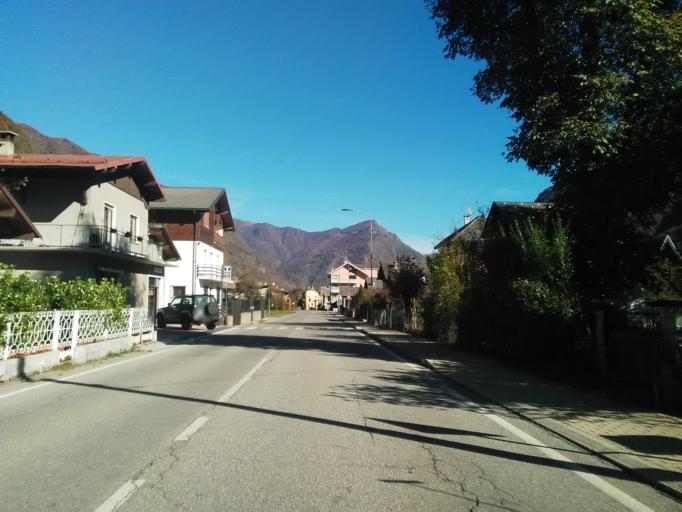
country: IT
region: Piedmont
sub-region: Provincia di Vercelli
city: Scopa
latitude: 45.7899
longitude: 8.1111
